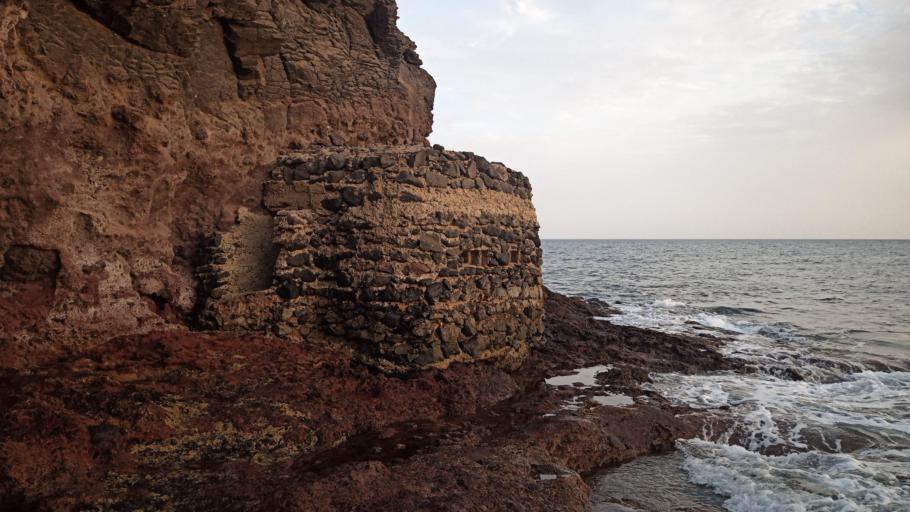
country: ES
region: Canary Islands
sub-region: Provincia de Las Palmas
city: Playa Blanca
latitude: 28.8438
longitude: -13.7801
